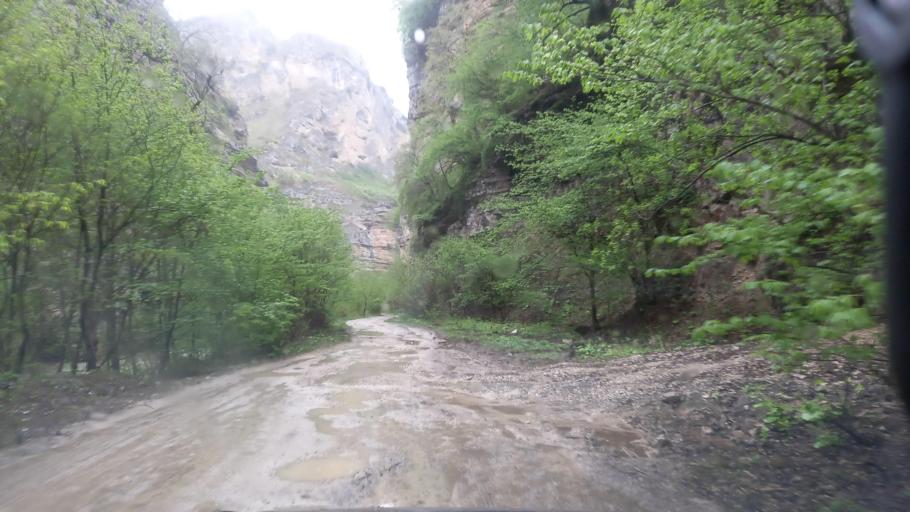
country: RU
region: Kabardino-Balkariya
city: Bylym
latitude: 43.5866
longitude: 43.0141
